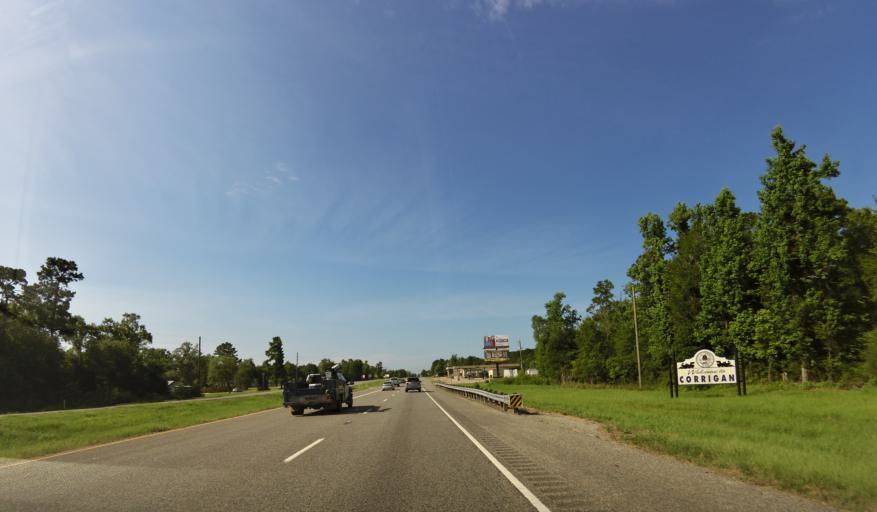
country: US
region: Texas
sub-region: Polk County
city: Corrigan
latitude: 31.0163
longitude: -94.8242
